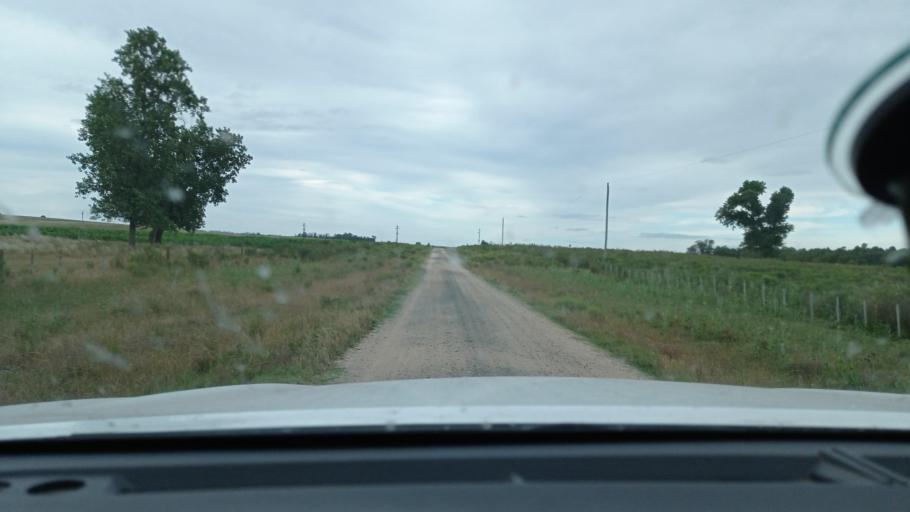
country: UY
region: Florida
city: Casupa
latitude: -34.1272
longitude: -55.7757
